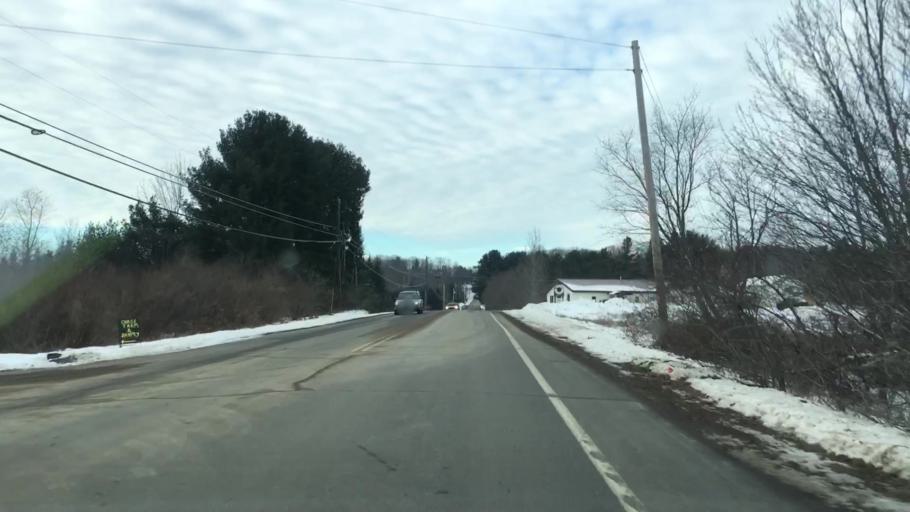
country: US
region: Maine
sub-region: Lincoln County
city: Whitefield
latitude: 44.2252
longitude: -69.6064
